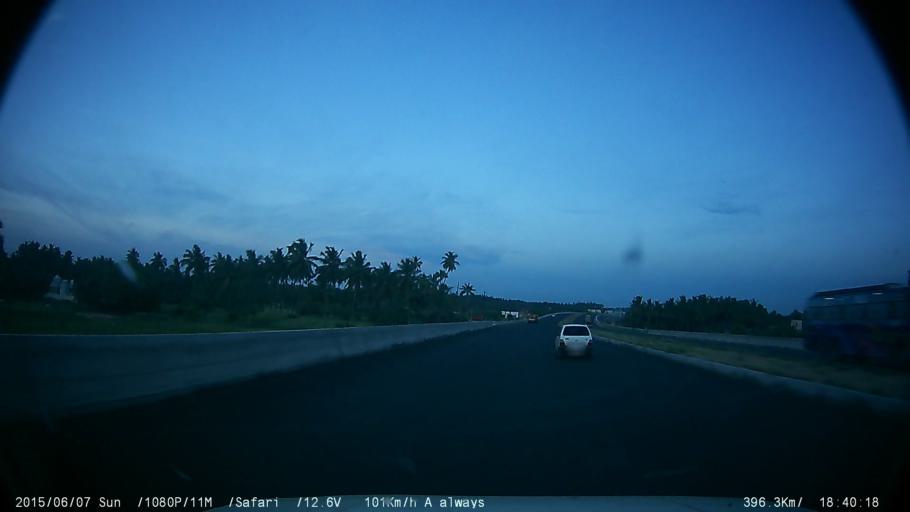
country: IN
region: Tamil Nadu
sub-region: Tiruppur
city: Avinashi
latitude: 11.2167
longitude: 77.3526
